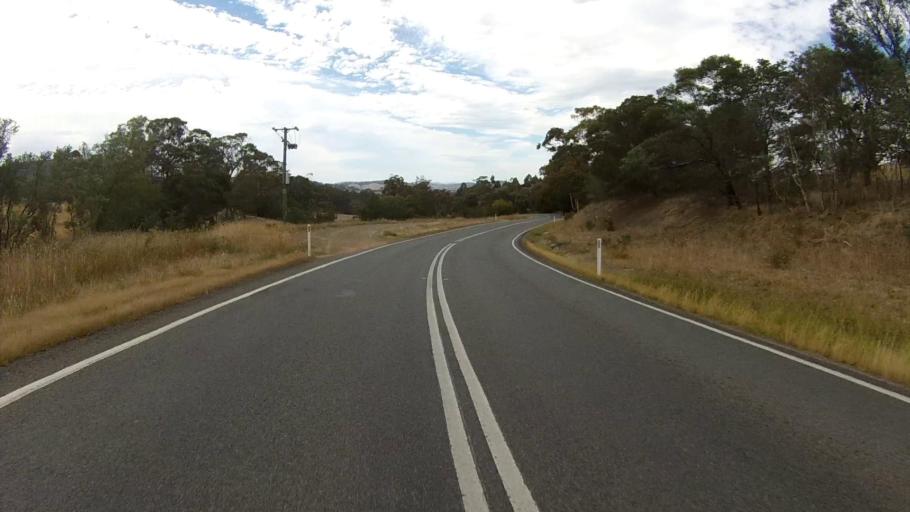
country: AU
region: Tasmania
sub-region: Sorell
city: Sorell
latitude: -42.7056
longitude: 147.4998
